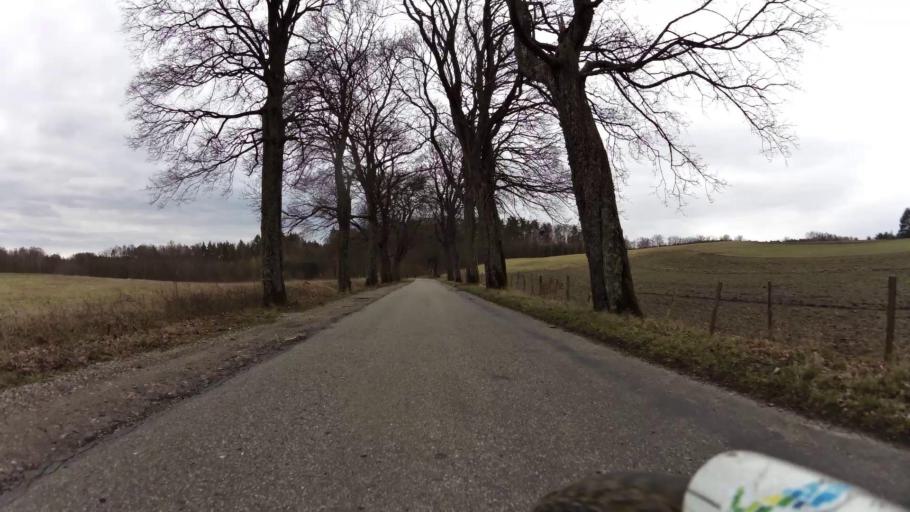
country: PL
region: Pomeranian Voivodeship
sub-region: Powiat bytowski
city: Trzebielino
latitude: 54.0999
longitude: 17.1320
